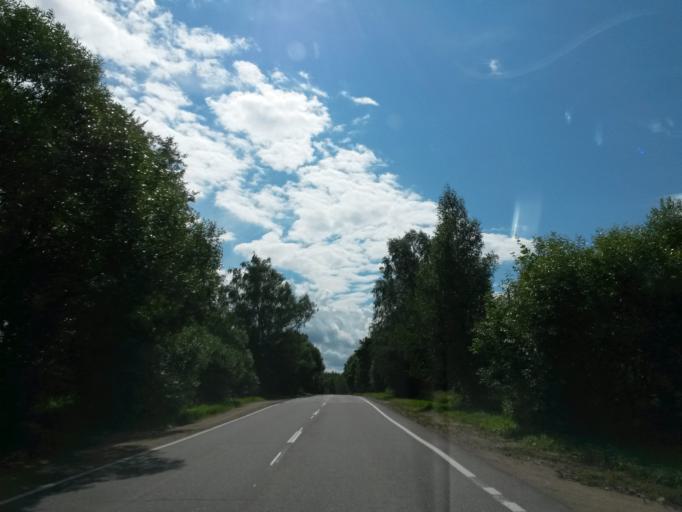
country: RU
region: Jaroslavl
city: Gavrilov-Yam
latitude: 57.2821
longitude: 39.9535
